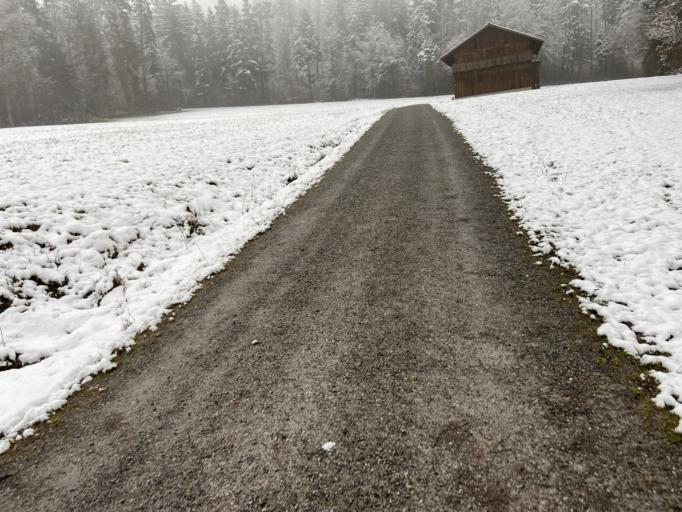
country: CH
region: Zurich
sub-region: Bezirk Meilen
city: Stafa
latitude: 47.2510
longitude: 8.7322
